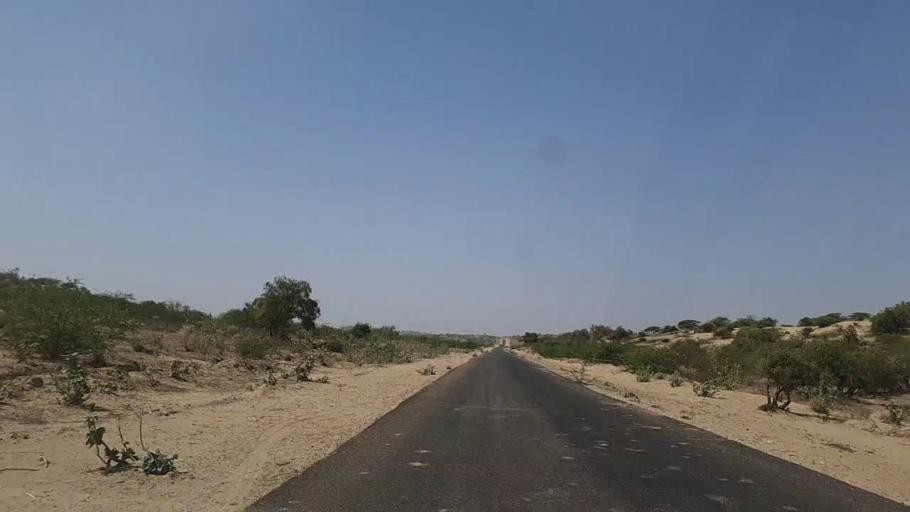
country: PK
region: Sindh
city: Diplo
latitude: 24.5565
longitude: 69.4488
